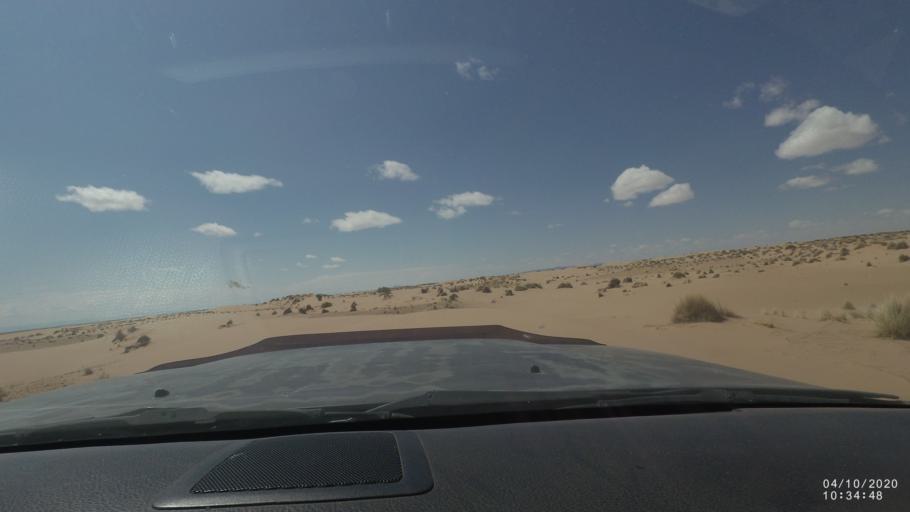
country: BO
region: Oruro
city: Poopo
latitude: -18.7047
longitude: -67.4770
